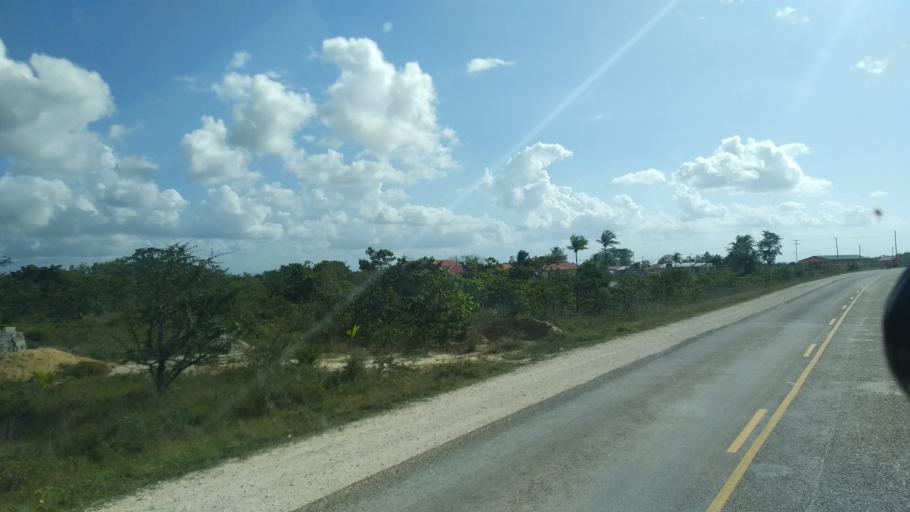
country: BZ
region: Belize
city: Belize City
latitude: 17.4068
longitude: -88.4561
